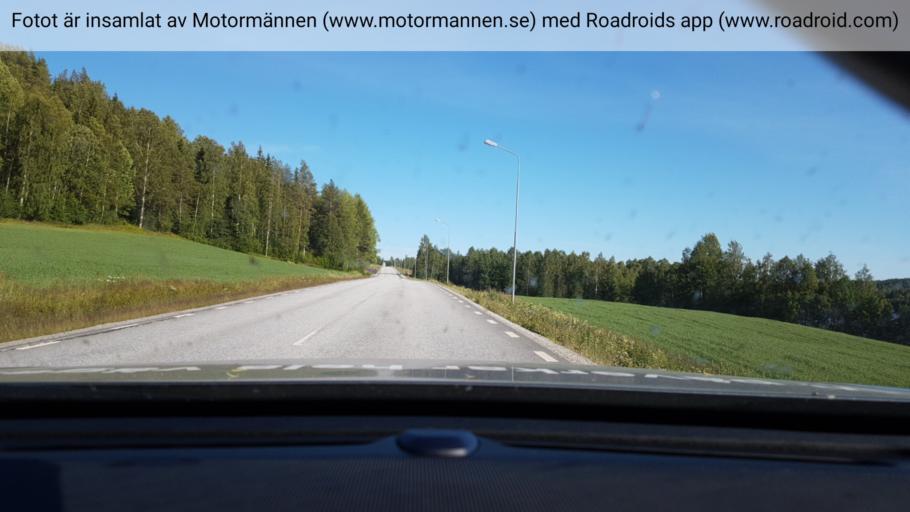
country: SE
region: Vaesterbotten
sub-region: Vindelns Kommun
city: Vindeln
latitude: 64.1351
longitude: 19.5293
